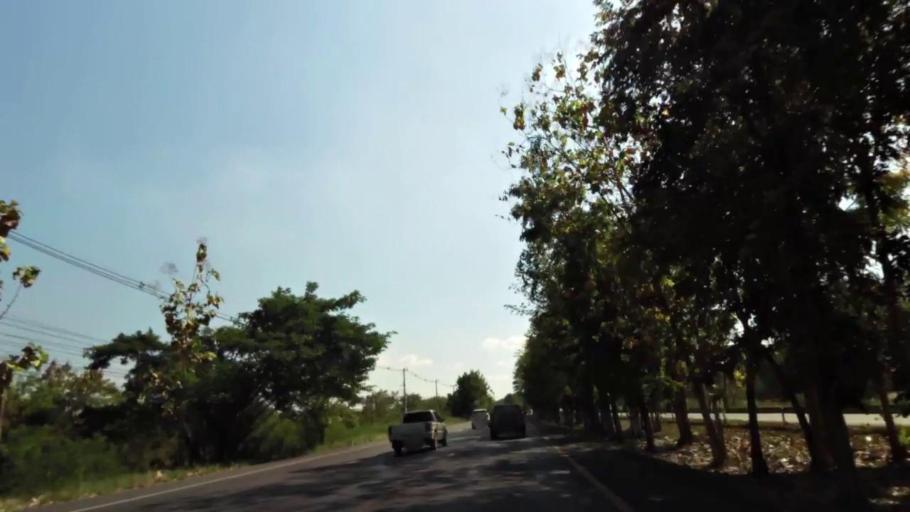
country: TH
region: Nakhon Sawan
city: Nakhon Sawan
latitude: 15.6481
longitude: 100.1343
